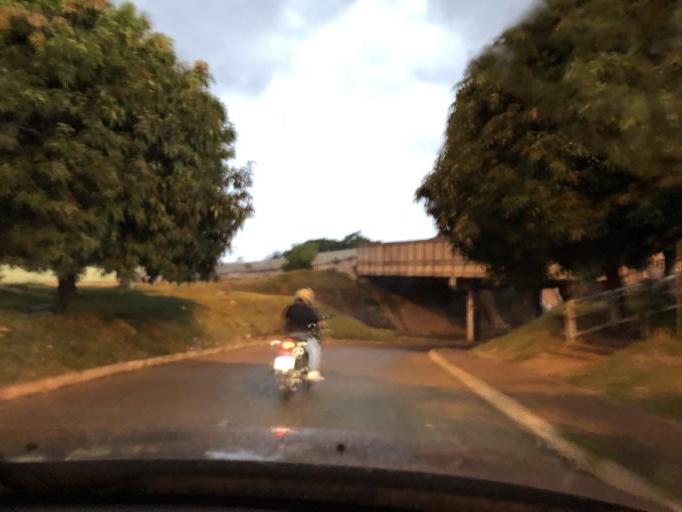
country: BR
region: Federal District
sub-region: Brasilia
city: Brasilia
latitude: -15.8086
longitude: -48.1190
